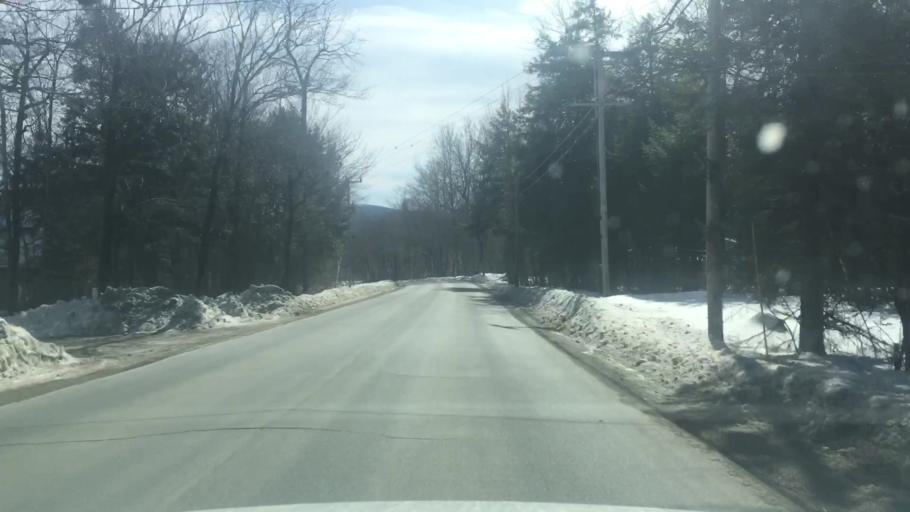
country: US
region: Maine
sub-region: Penobscot County
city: Holden
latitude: 44.7607
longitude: -68.6416
